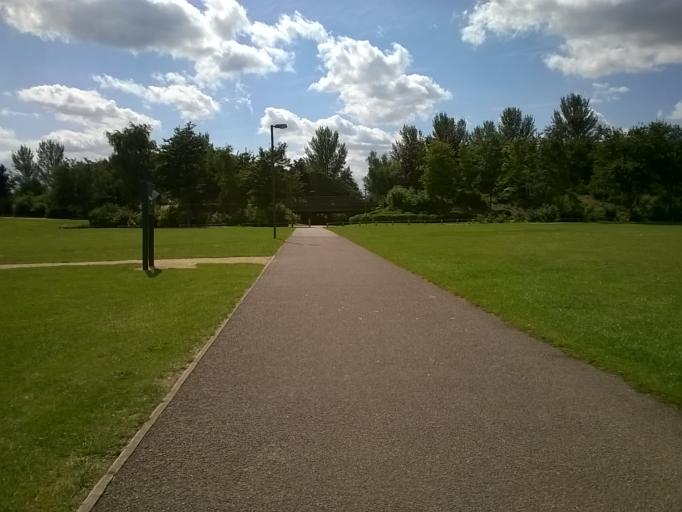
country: GB
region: England
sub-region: Milton Keynes
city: Broughton
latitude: 52.0558
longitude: -0.7243
